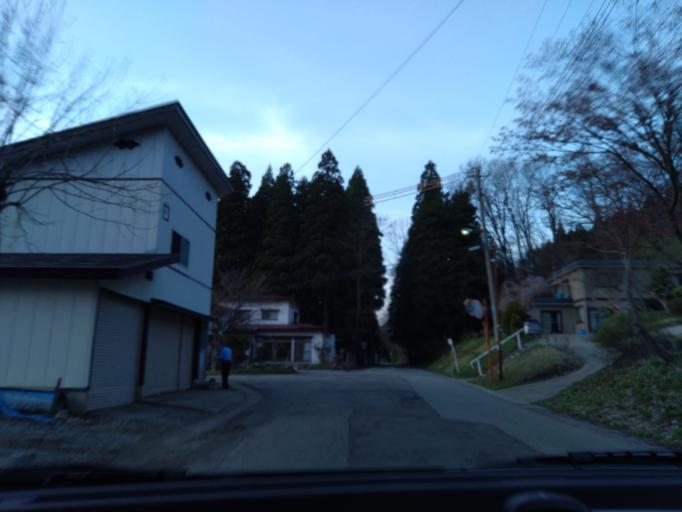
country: JP
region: Akita
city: Kakunodatemachi
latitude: 39.5874
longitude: 140.5763
